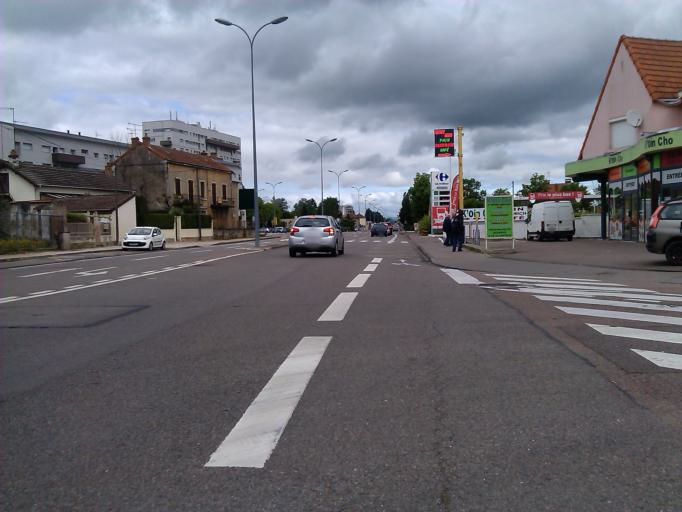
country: FR
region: Bourgogne
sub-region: Departement de Saone-et-Loire
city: Chalon-sur-Saone
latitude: 46.7974
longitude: 4.8477
